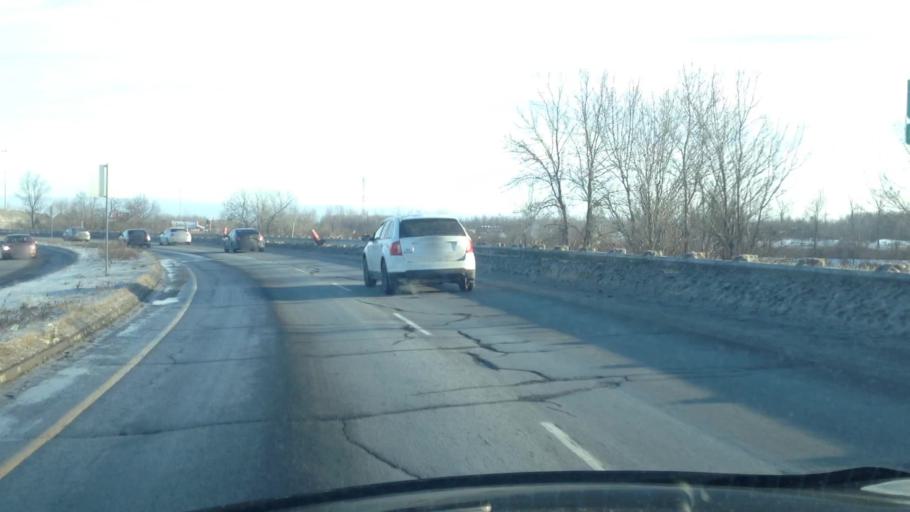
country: CA
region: Quebec
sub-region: Laurentides
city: Saint-Jerome
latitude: 45.7451
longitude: -74.0065
